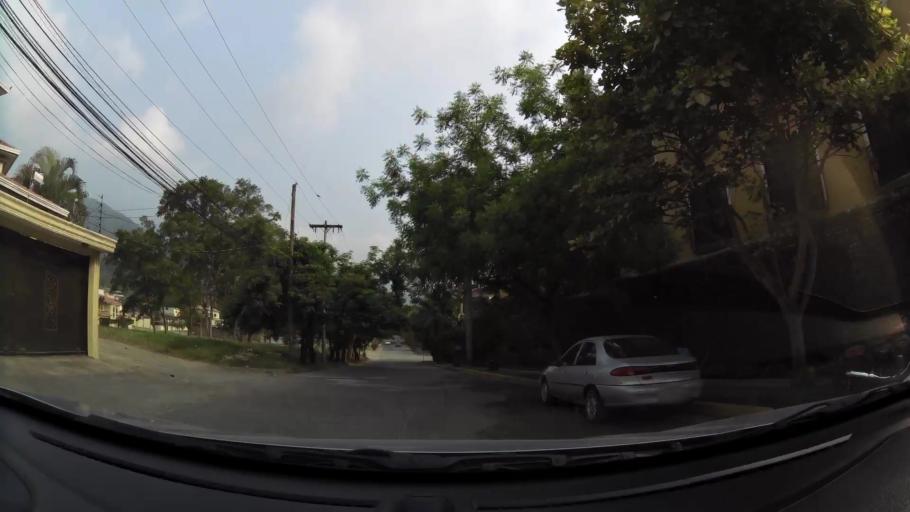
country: HN
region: Cortes
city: Armenta
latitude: 15.4889
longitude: -88.0438
